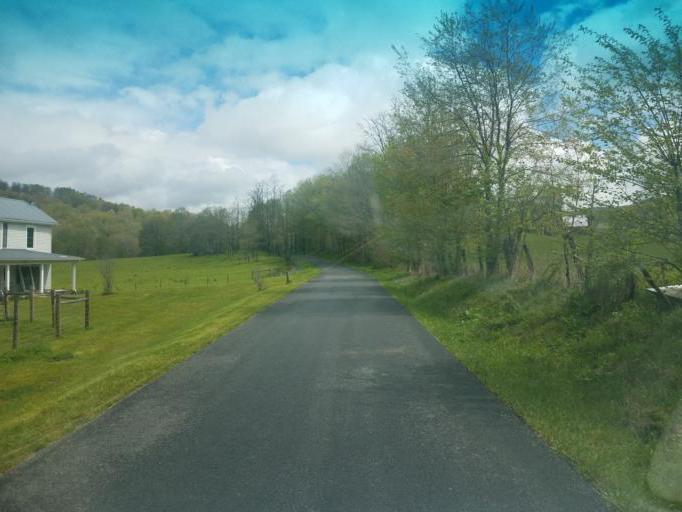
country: US
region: Virginia
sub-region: Smyth County
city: Atkins
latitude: 36.9432
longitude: -81.4169
